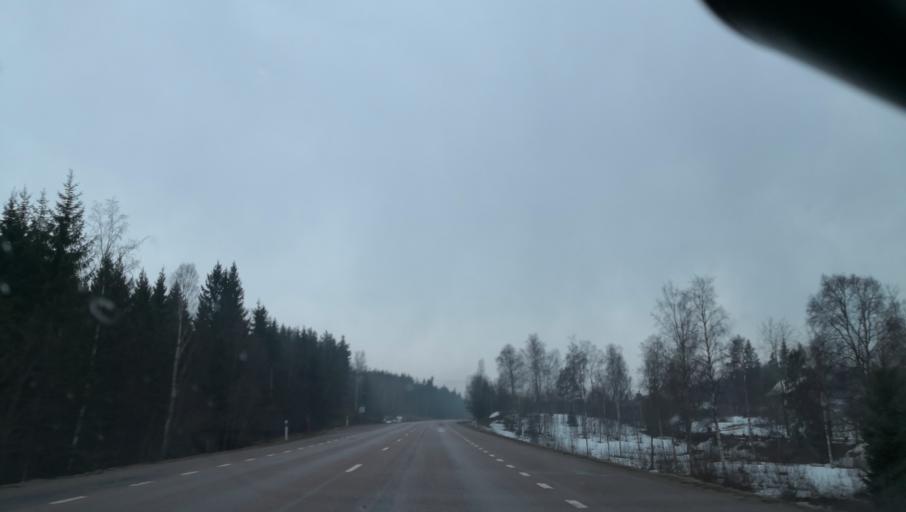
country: SE
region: Gaevleborg
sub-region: Nordanstigs Kommun
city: Bergsjoe
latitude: 62.0407
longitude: 17.2635
